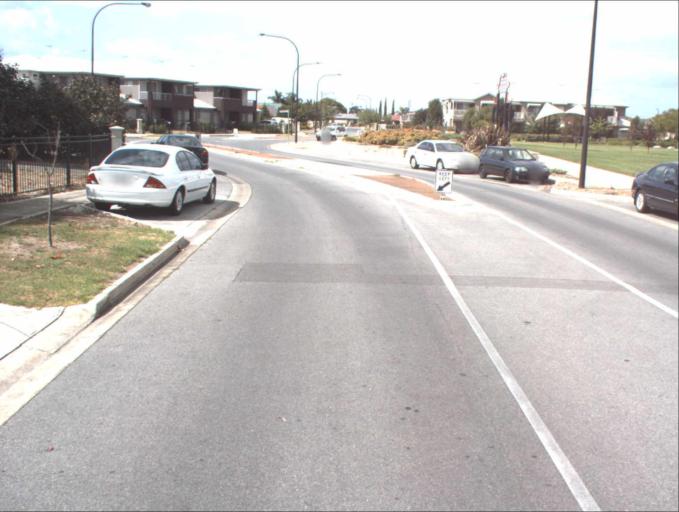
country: AU
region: South Australia
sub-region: Charles Sturt
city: Woodville
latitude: -34.8696
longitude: 138.5621
